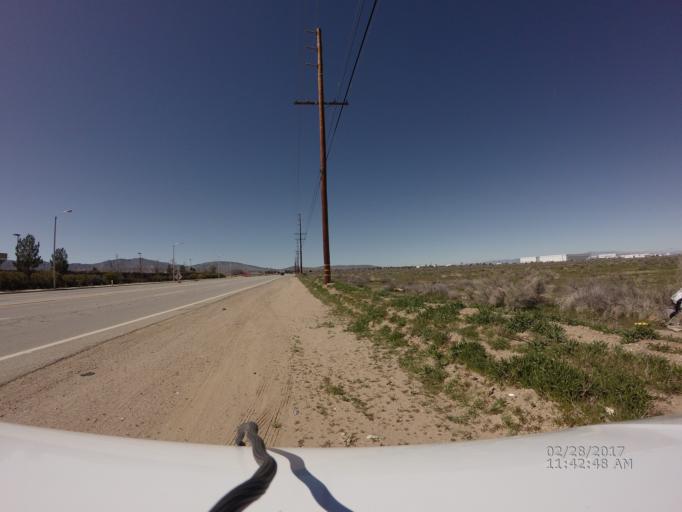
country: US
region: California
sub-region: Los Angeles County
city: Palmdale
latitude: 34.6022
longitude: -118.1060
